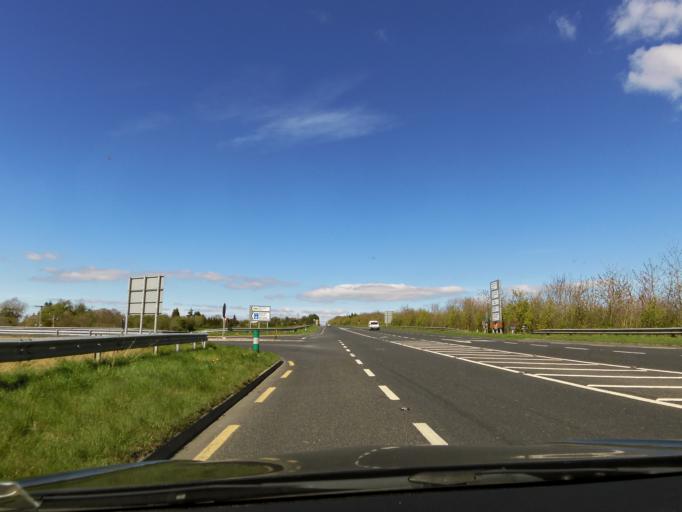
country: IE
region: Leinster
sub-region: Kildare
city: Moone
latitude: 53.0017
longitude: -6.8057
